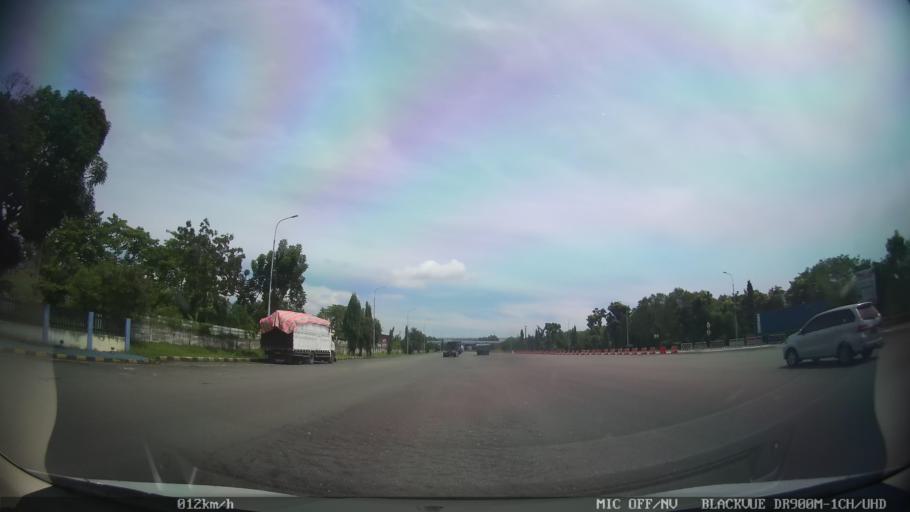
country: ID
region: North Sumatra
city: Labuhan Deli
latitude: 3.7301
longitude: 98.6808
